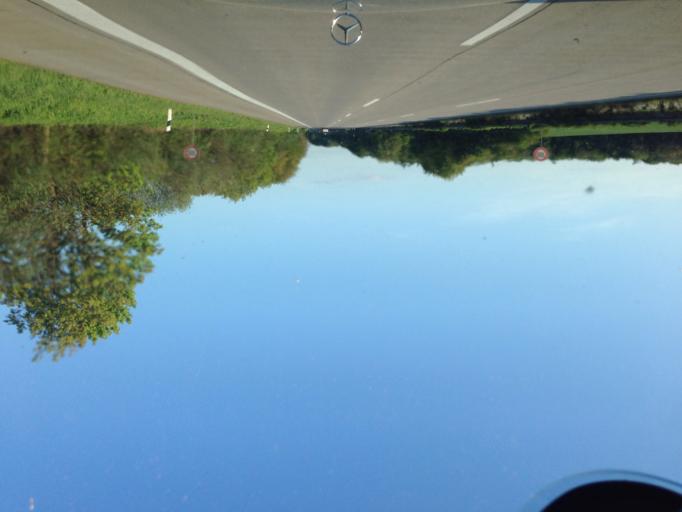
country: DE
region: Schleswig-Holstein
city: Lasbek
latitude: 53.7427
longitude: 10.3602
